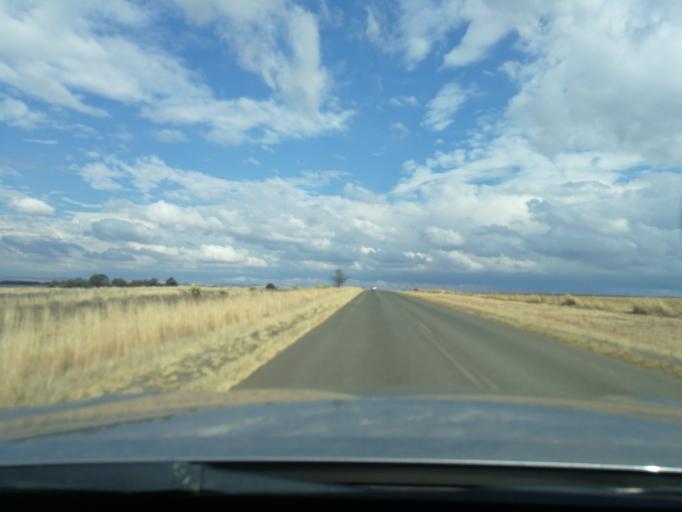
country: ZA
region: Orange Free State
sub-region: Fezile Dabi District Municipality
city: Frankfort
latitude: -27.4402
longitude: 28.5135
